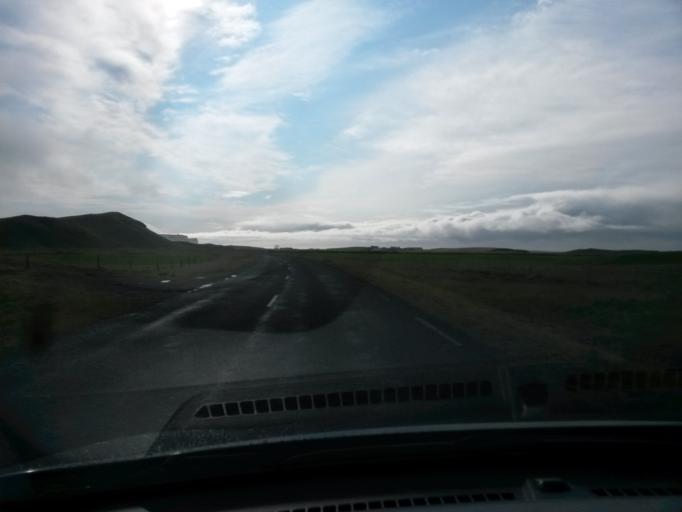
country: IS
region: South
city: Vestmannaeyjar
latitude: 63.4349
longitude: -19.1919
